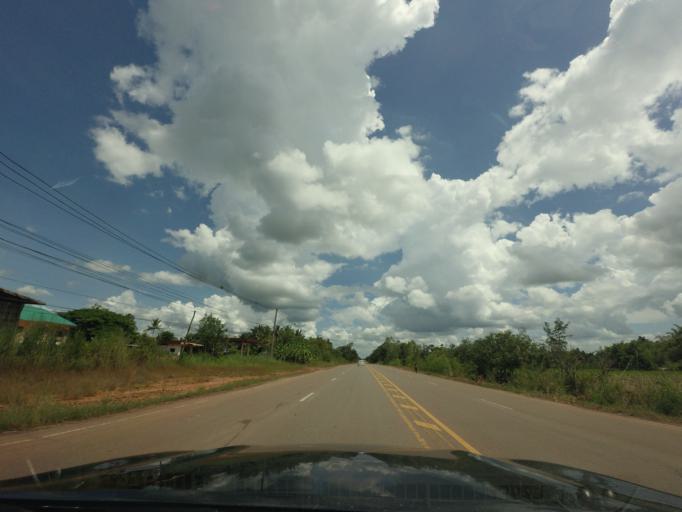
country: TH
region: Changwat Udon Thani
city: Ban Dung
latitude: 17.6816
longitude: 103.2253
